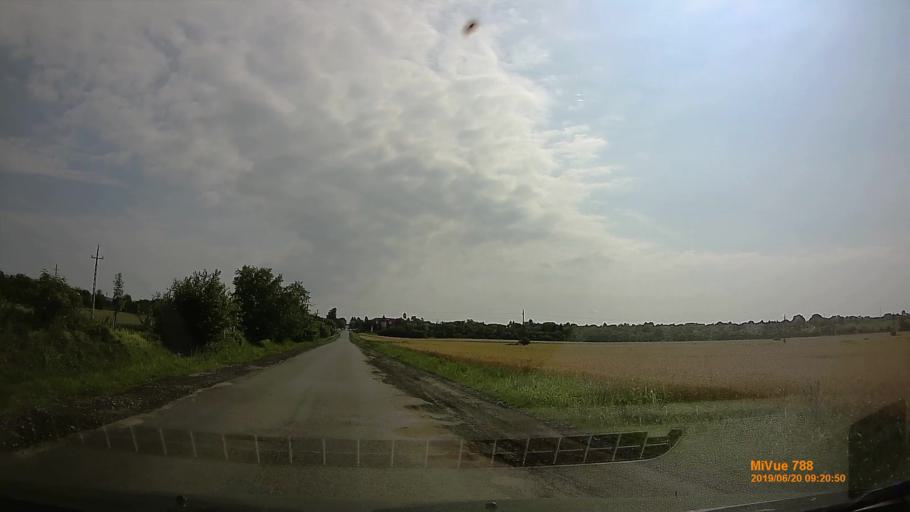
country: HU
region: Baranya
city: Hosszuheteny
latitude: 46.1139
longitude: 18.3278
